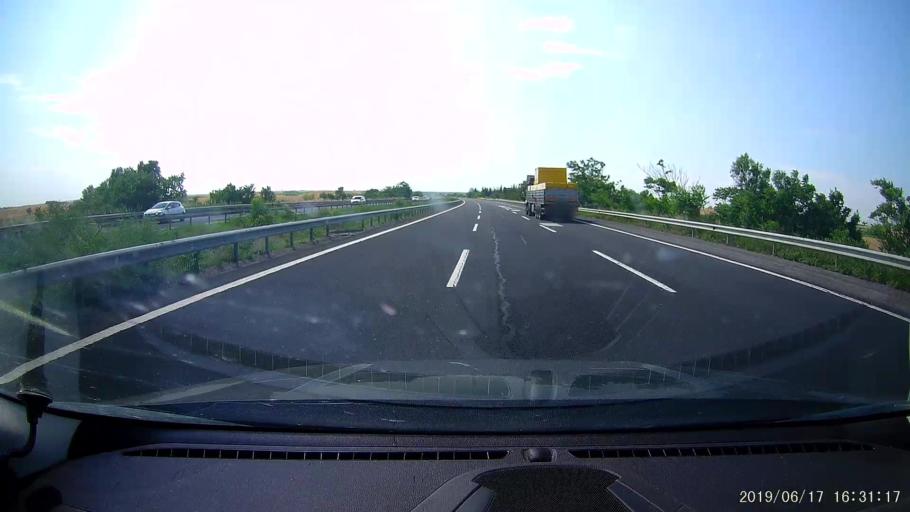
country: TR
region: Tekirdag
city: Beyazkoy
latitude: 41.3603
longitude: 27.6326
